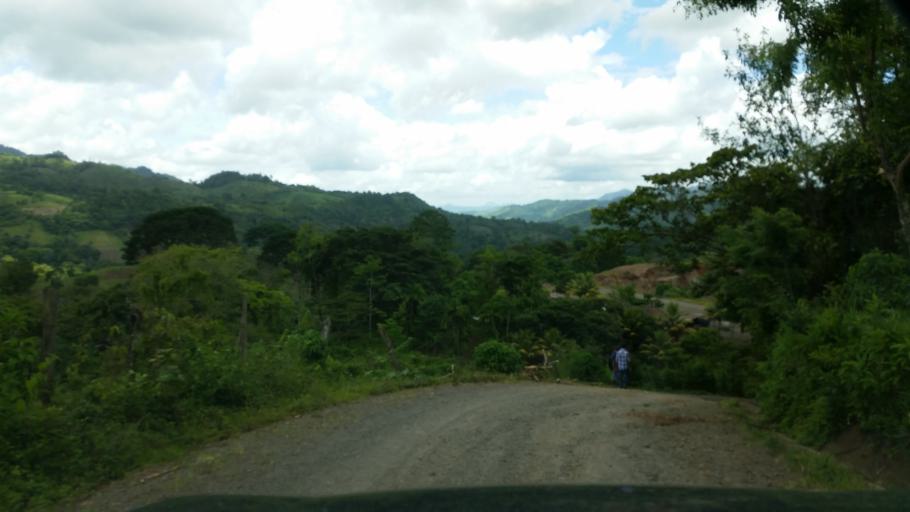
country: NI
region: Atlantico Norte (RAAN)
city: Waslala
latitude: 13.2649
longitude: -85.6200
